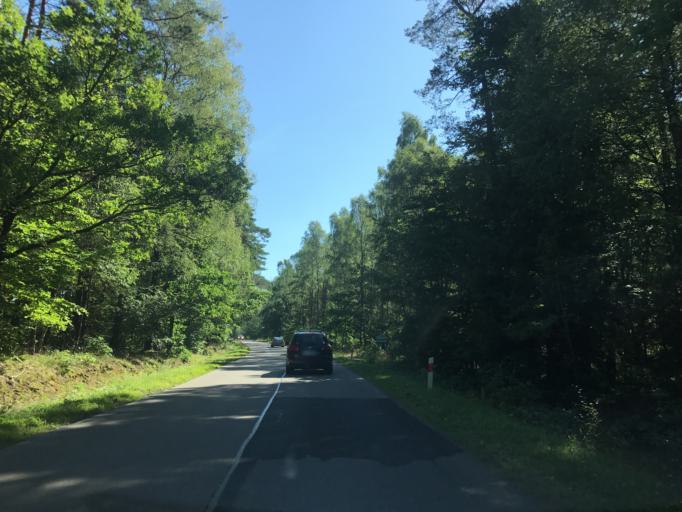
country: PL
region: Pomeranian Voivodeship
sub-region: Powiat bytowski
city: Czarna Dabrowka
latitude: 54.3392
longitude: 17.6514
